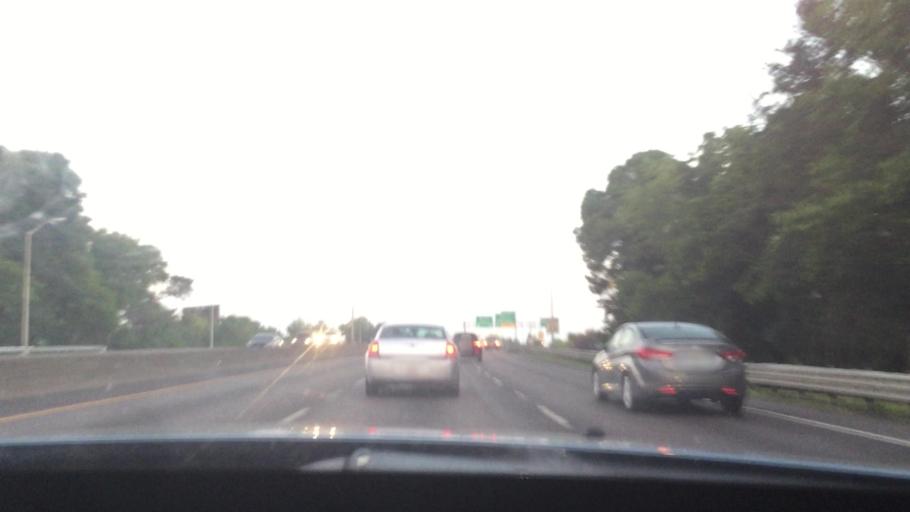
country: US
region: Louisiana
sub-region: East Baton Rouge Parish
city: Baton Rouge
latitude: 30.4300
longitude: -91.1730
